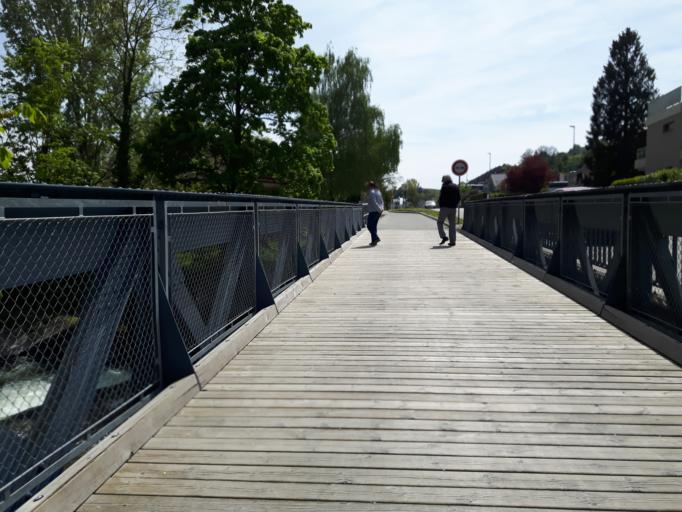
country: CH
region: Neuchatel
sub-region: Boudry District
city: Cortaillod
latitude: 46.9523
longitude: 6.8533
